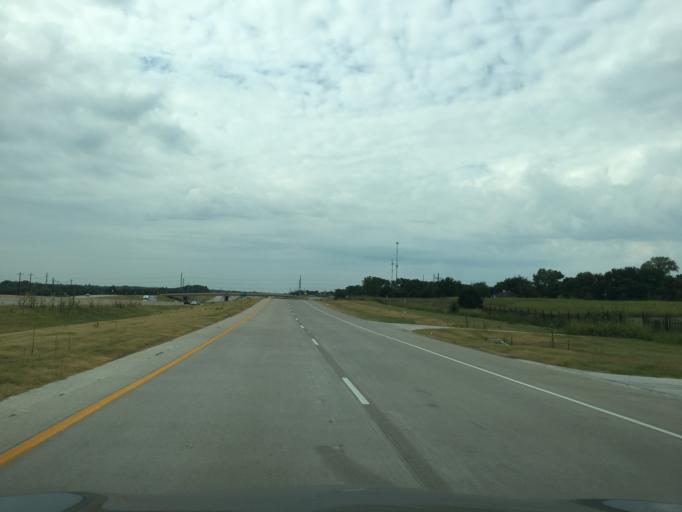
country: US
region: Texas
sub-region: Collin County
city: Melissa
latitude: 33.3241
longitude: -96.5907
